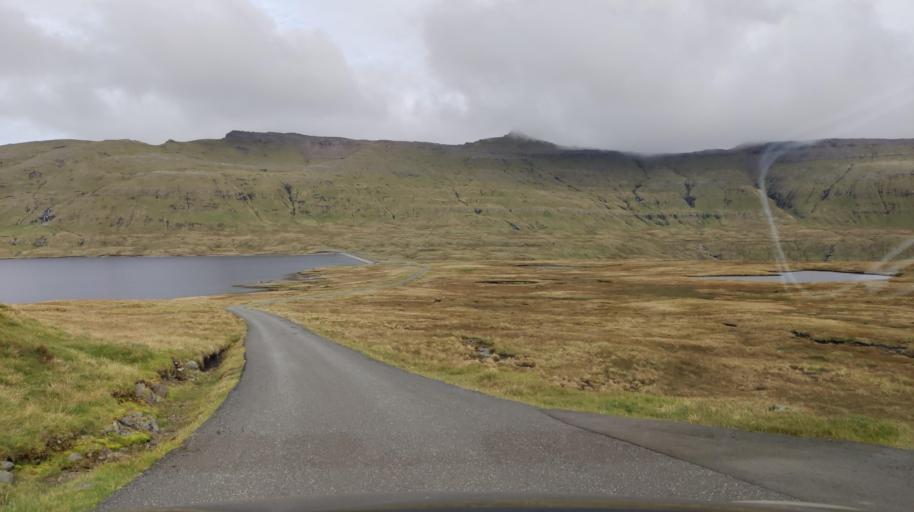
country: FO
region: Streymoy
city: Vestmanna
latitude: 62.1621
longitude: -7.0946
